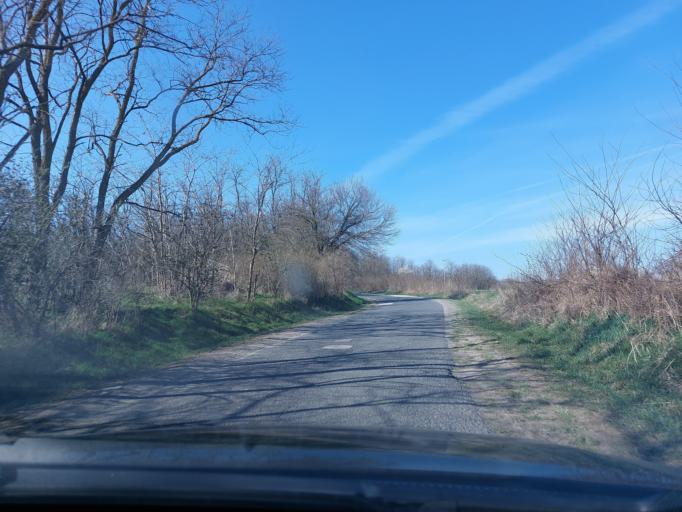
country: HU
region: Veszprem
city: Devecser
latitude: 47.1380
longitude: 17.3963
